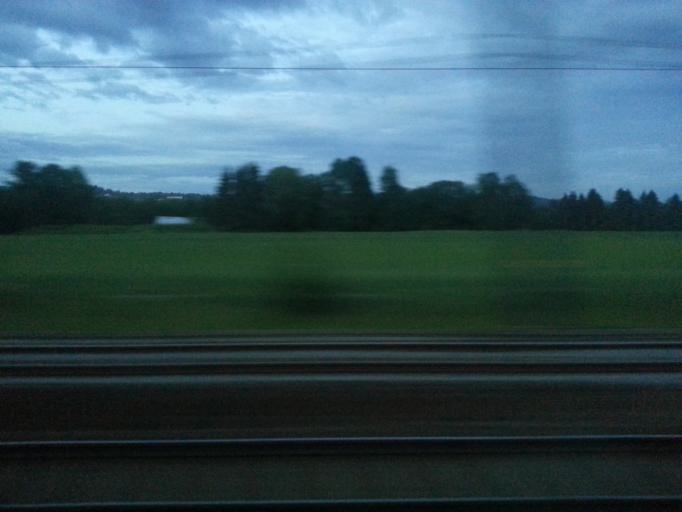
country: NO
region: Akershus
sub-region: Skedsmo
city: Leirsund
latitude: 59.9823
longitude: 11.0739
